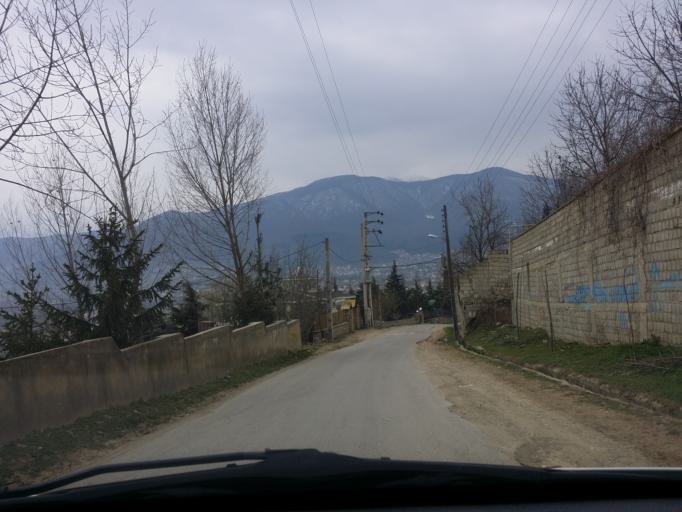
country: IR
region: Mazandaran
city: `Abbasabad
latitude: 36.5337
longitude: 51.1613
